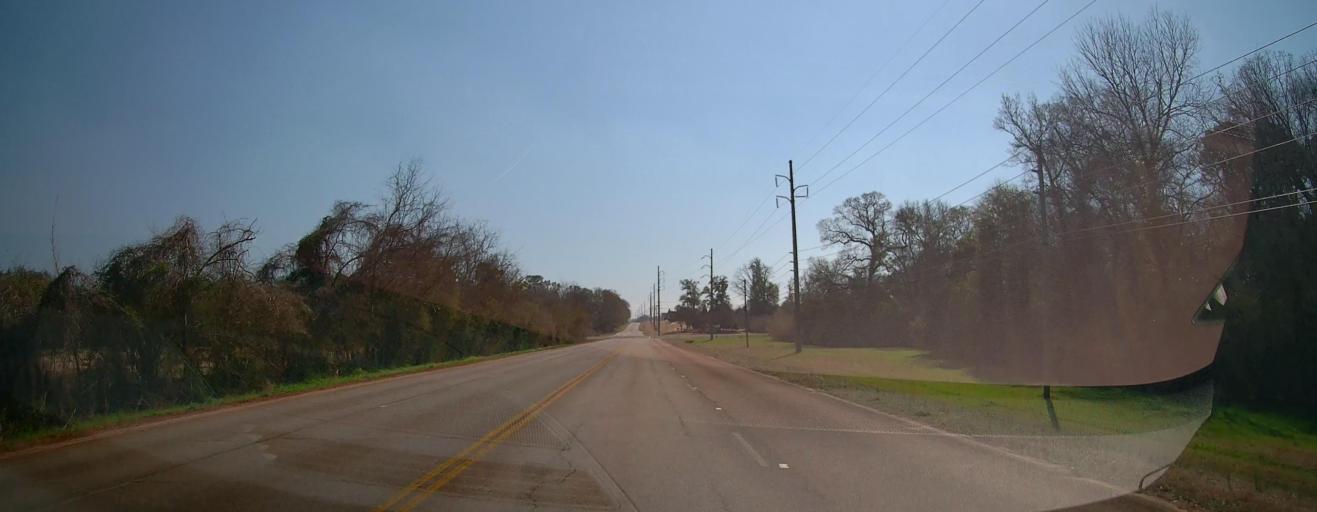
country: US
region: Georgia
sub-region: Houston County
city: Perry
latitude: 32.4829
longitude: -83.7589
